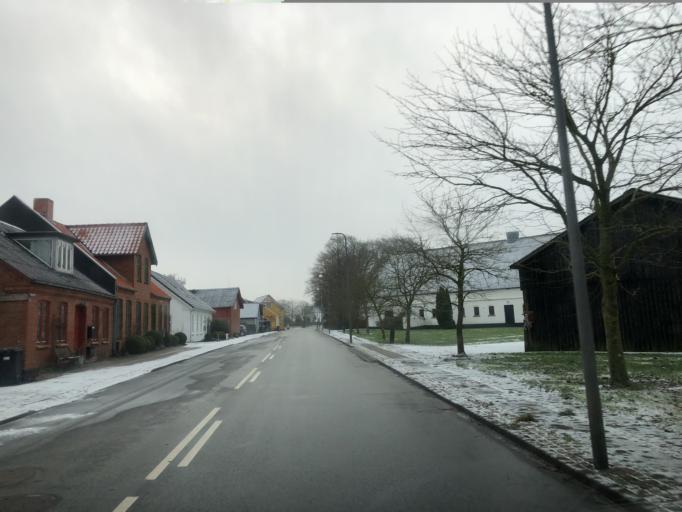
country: DK
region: South Denmark
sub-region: Vejle Kommune
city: Jelling
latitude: 55.7586
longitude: 9.4165
